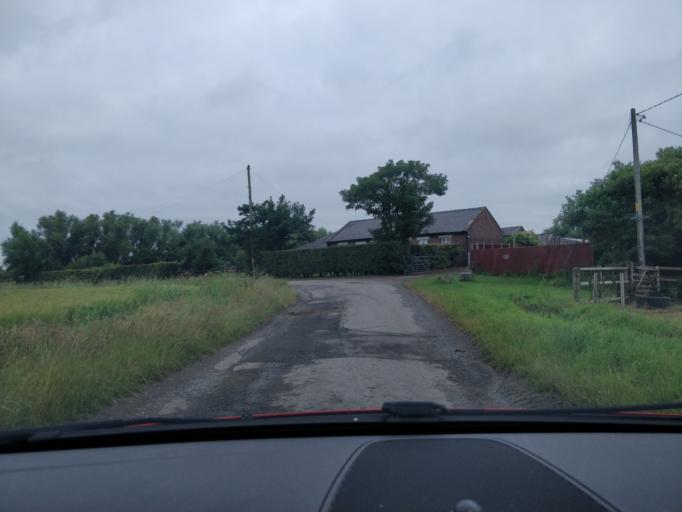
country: GB
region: England
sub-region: Lancashire
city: Banks
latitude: 53.6675
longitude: -2.9384
